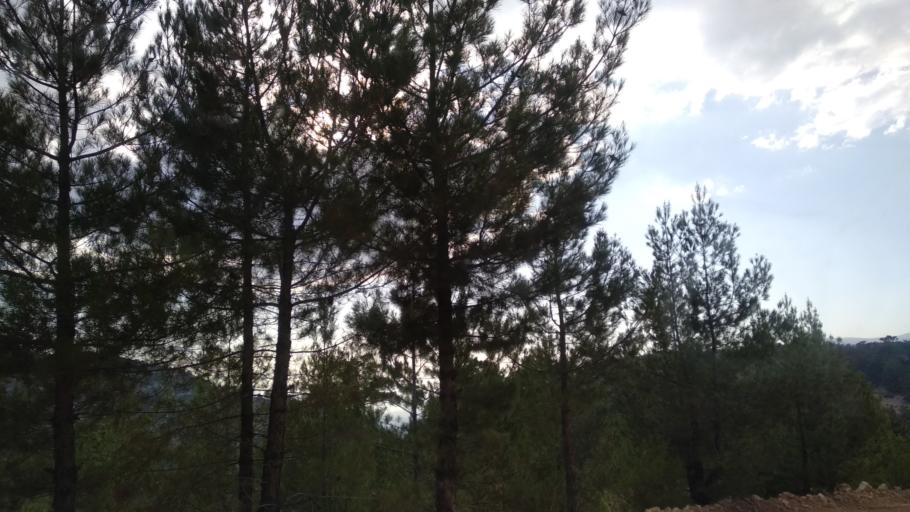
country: TR
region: Mersin
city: Sarikavak
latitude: 36.5993
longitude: 33.7129
